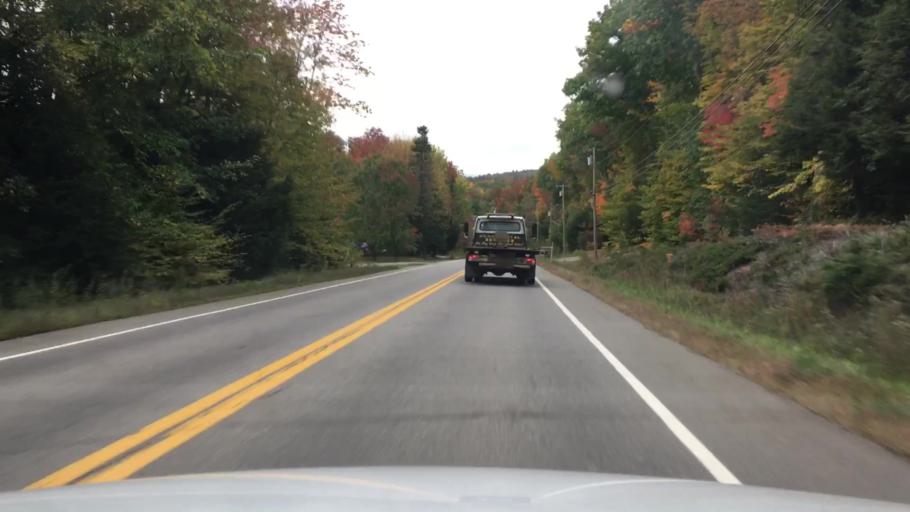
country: US
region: Maine
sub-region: Kennebec County
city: Oakland
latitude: 44.5603
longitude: -69.7444
